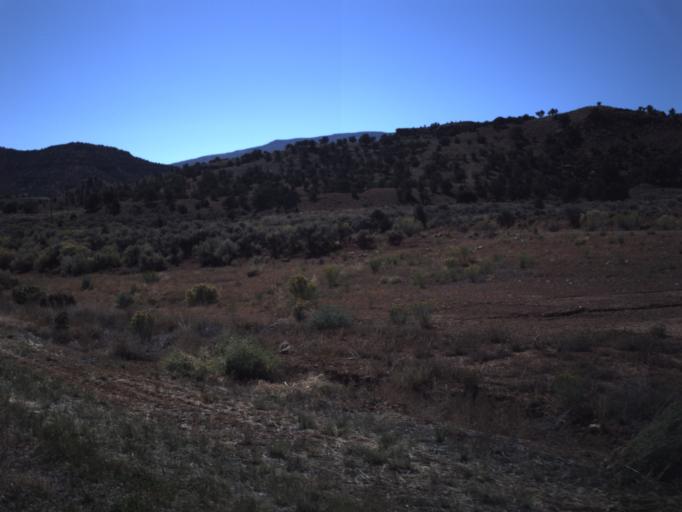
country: US
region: Utah
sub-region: Wayne County
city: Loa
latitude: 38.2769
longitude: -111.3845
